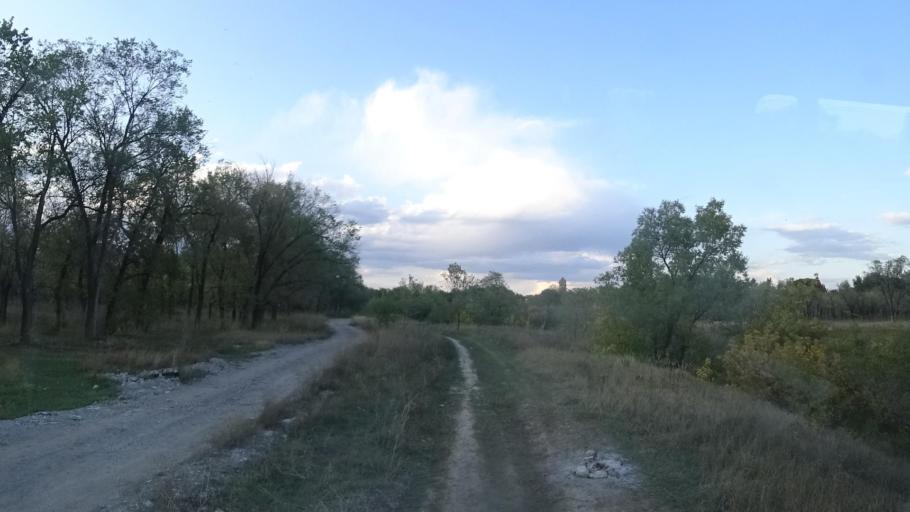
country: KZ
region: Almaty Oblysy
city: Pervomayskiy
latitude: 43.3344
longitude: 76.9995
